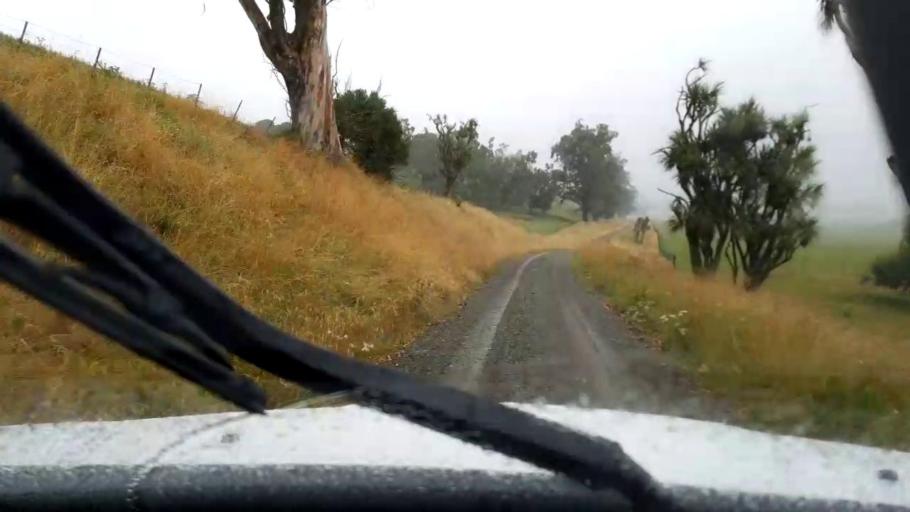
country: NZ
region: Canterbury
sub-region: Timaru District
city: Pleasant Point
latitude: -44.1902
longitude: 171.1034
